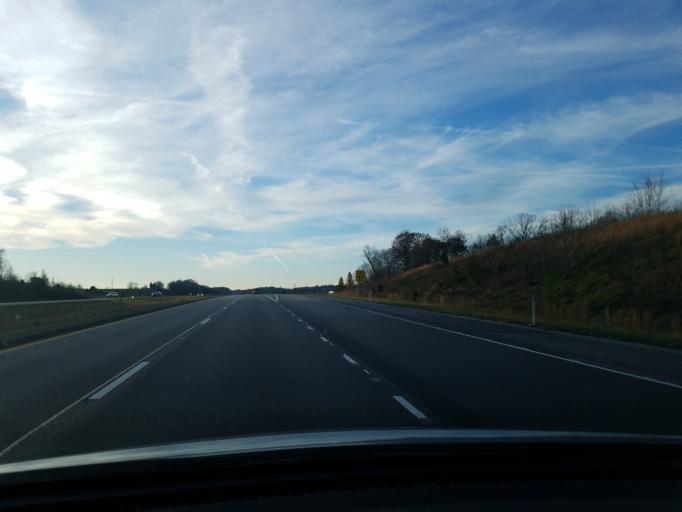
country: US
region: Indiana
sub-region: Dubois County
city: Ferdinand
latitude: 38.2058
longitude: -86.8579
